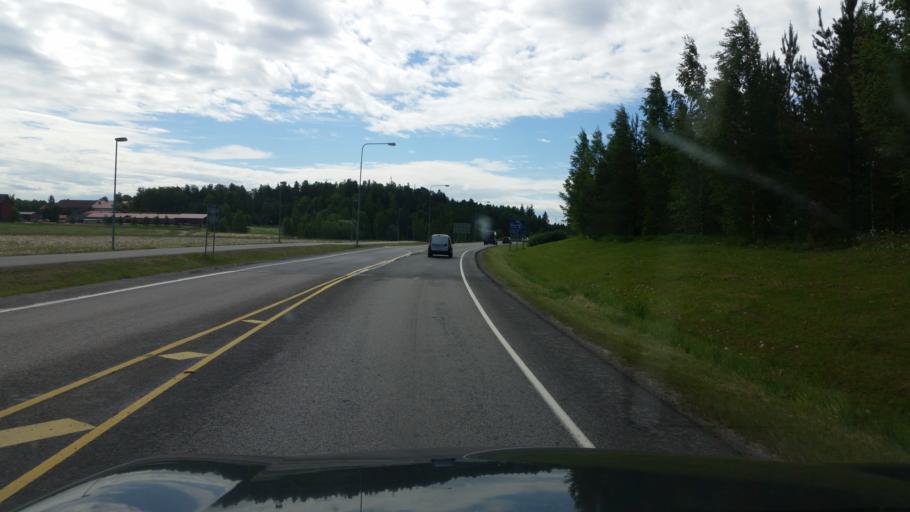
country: FI
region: Varsinais-Suomi
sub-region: Turku
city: Kaarina
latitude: 60.4070
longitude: 22.3867
